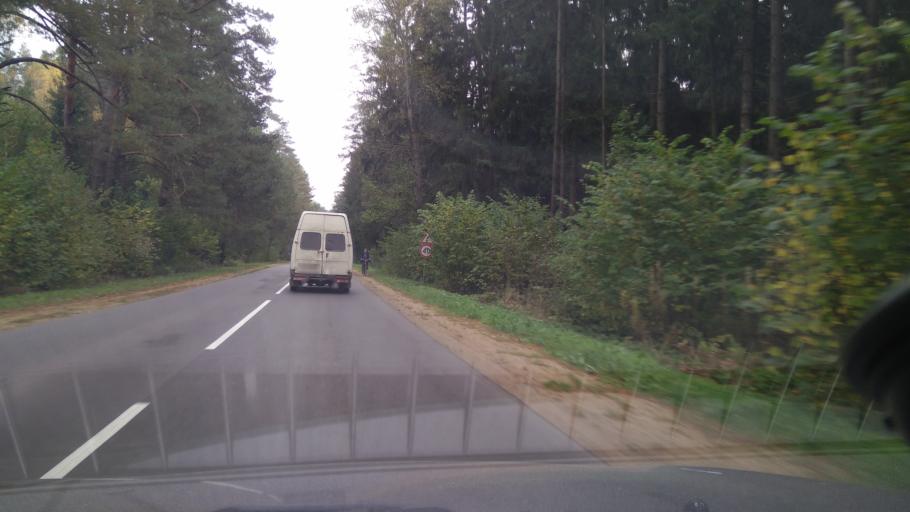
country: BY
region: Minsk
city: Rudzyensk
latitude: 53.6132
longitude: 27.7870
